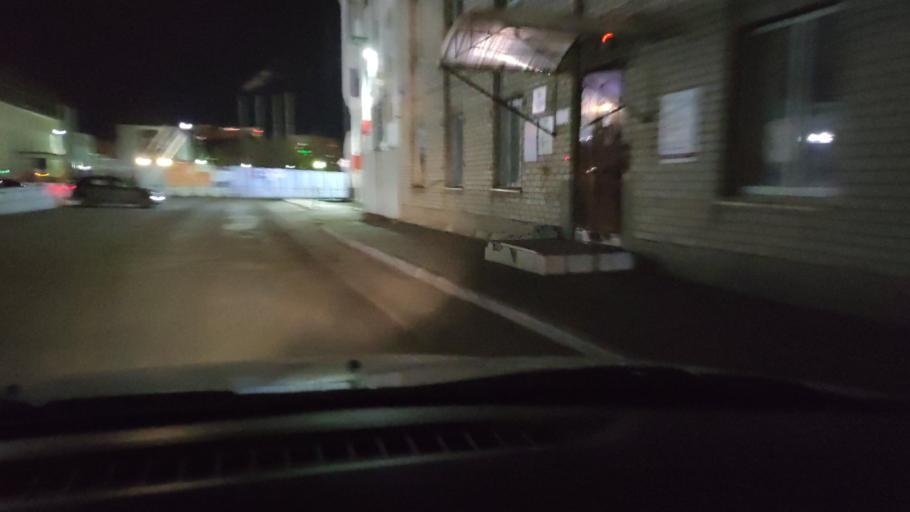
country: RU
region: Perm
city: Perm
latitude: 57.9898
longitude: 56.2058
